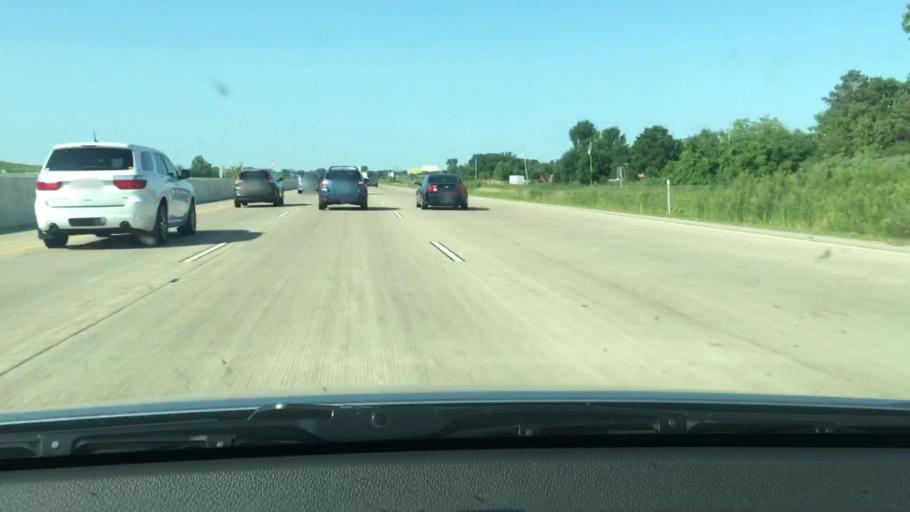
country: US
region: Wisconsin
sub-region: Winnebago County
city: Oshkosh
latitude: 44.0933
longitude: -88.5485
